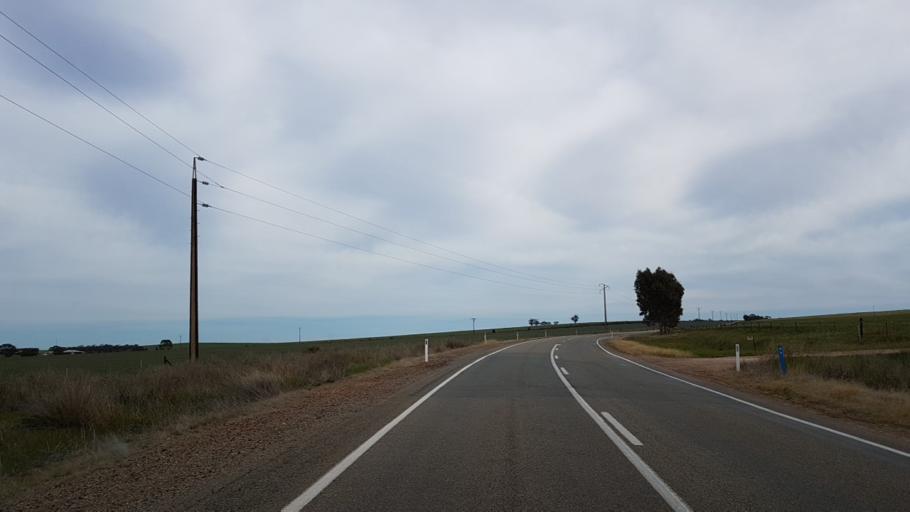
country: AU
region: South Australia
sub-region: Port Pirie City and Dists
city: Crystal Brook
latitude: -33.2741
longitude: 138.3126
